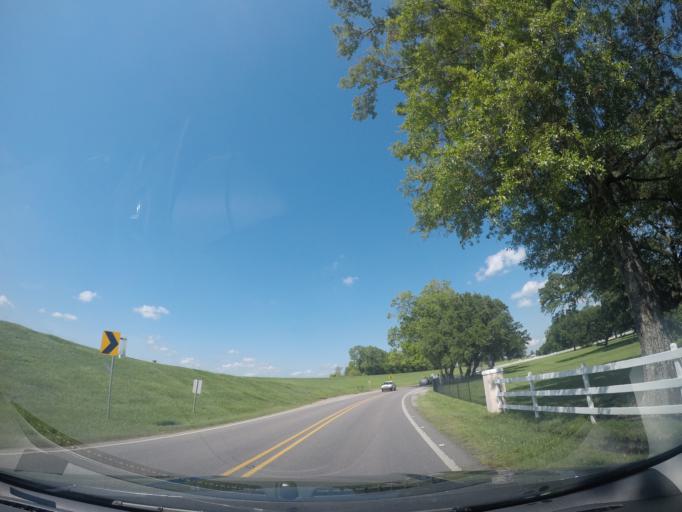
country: US
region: Louisiana
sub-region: Saint James Parish
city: Convent
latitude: 30.0067
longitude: -90.7769
